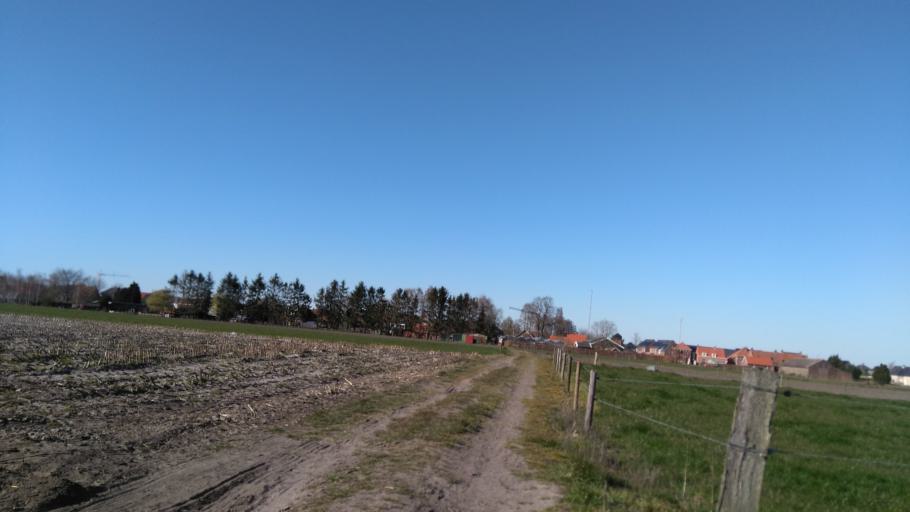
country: NL
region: North Brabant
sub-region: Gemeente Baarle-Nassau
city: Baarle-Nassau
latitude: 51.4391
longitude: 4.9364
